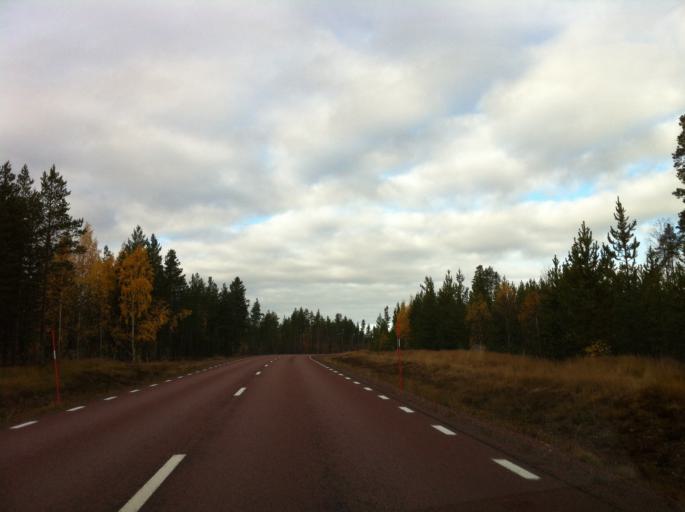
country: SE
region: Dalarna
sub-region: Alvdalens Kommun
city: AElvdalen
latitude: 61.5501
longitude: 13.3292
